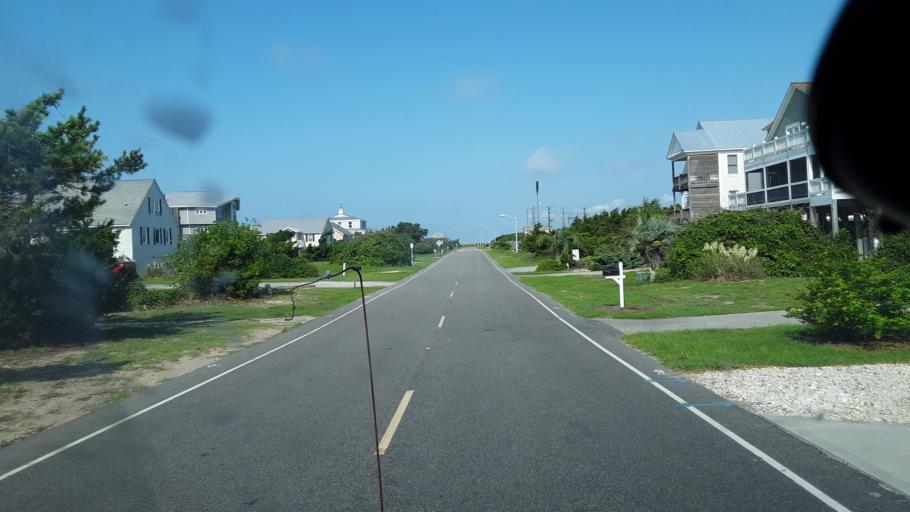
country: US
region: North Carolina
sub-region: Brunswick County
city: Southport
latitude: 33.8966
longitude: -78.0505
